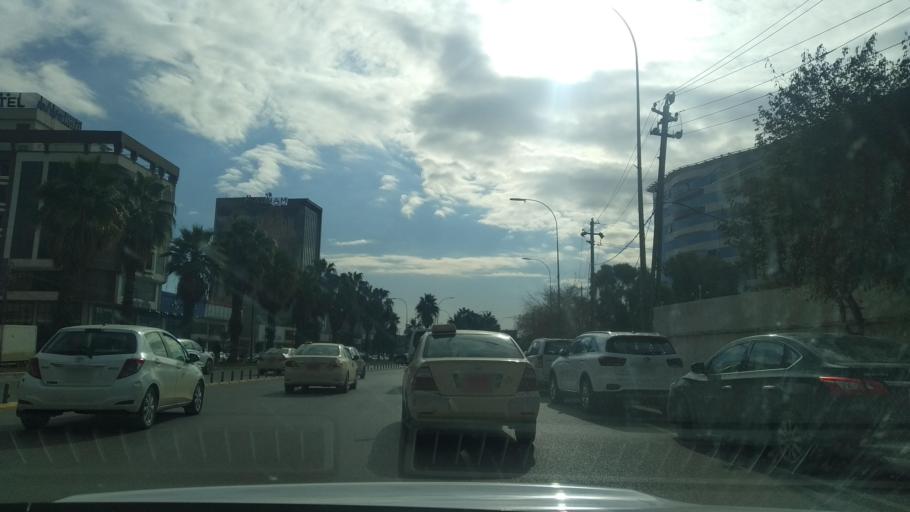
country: IQ
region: Arbil
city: Erbil
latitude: 36.1998
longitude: 44.0219
